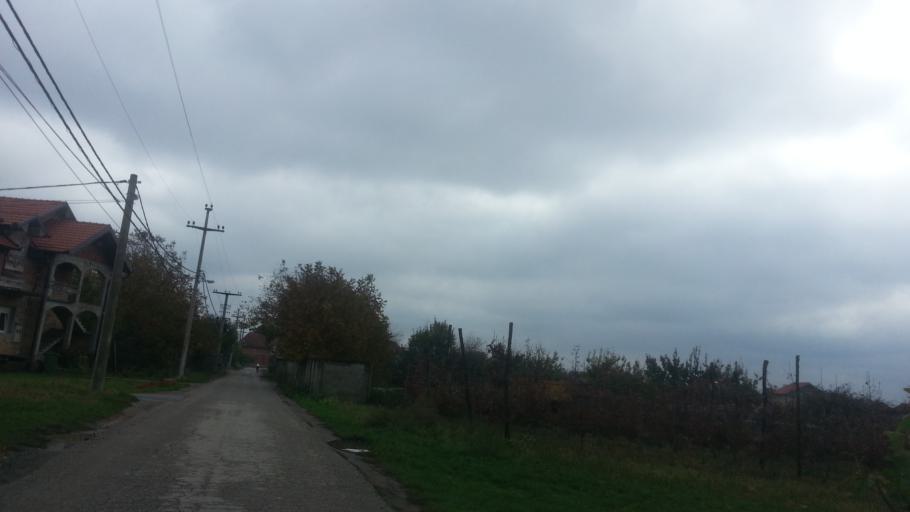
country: RS
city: Novi Banovci
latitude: 44.9156
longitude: 20.2825
